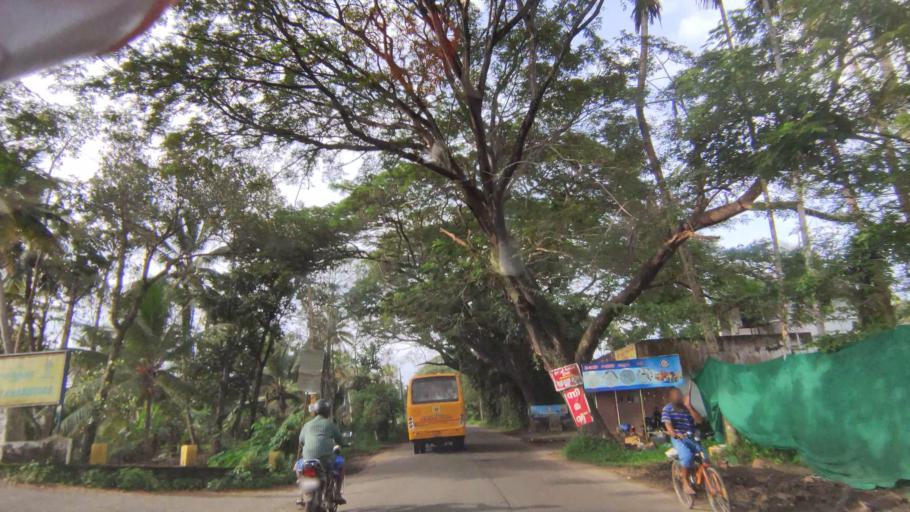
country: IN
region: Kerala
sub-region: Kottayam
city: Kottayam
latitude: 9.6056
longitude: 76.4331
